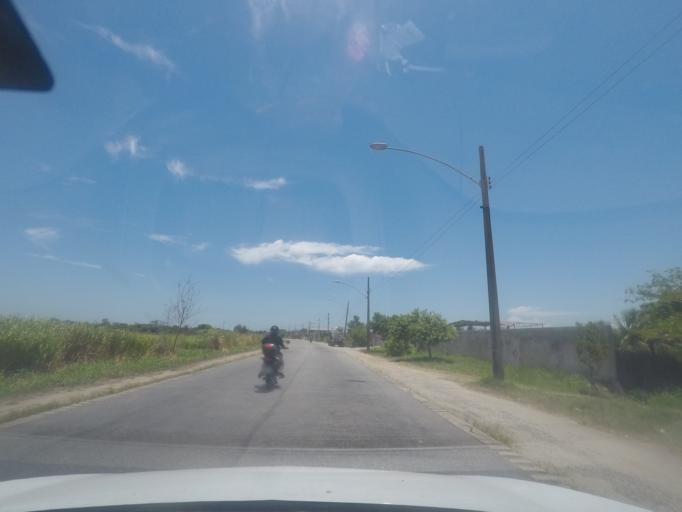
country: BR
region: Rio de Janeiro
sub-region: Itaguai
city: Itaguai
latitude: -22.8985
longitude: -43.6883
